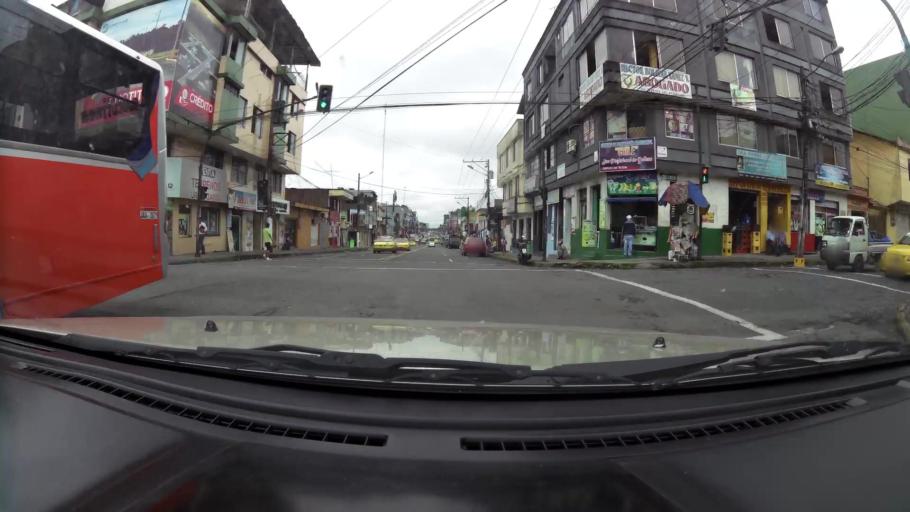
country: EC
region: Santo Domingo de los Tsachilas
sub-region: Canton Santo Domingo de los Colorados
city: Santo Domingo de los Colorados
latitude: -0.2521
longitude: -79.1683
